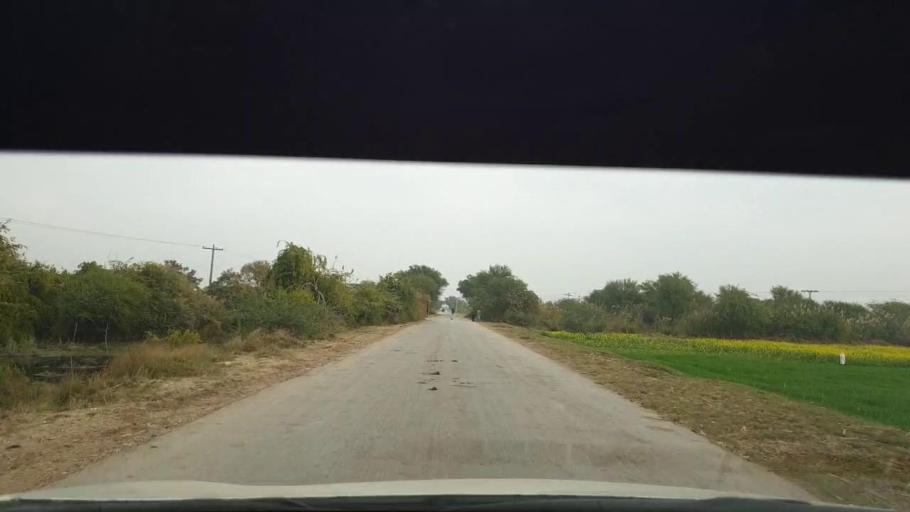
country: PK
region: Sindh
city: Berani
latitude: 25.7772
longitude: 68.8973
